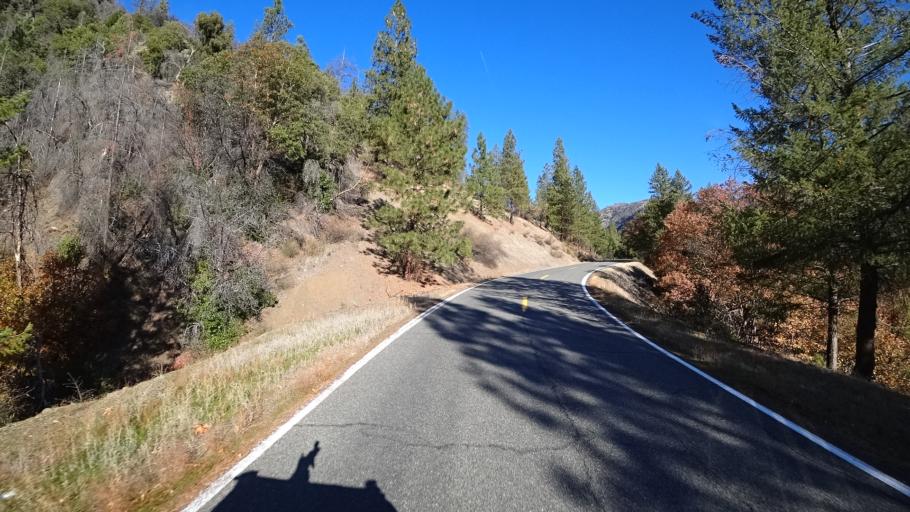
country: US
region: California
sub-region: Siskiyou County
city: Yreka
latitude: 41.8952
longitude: -122.8263
